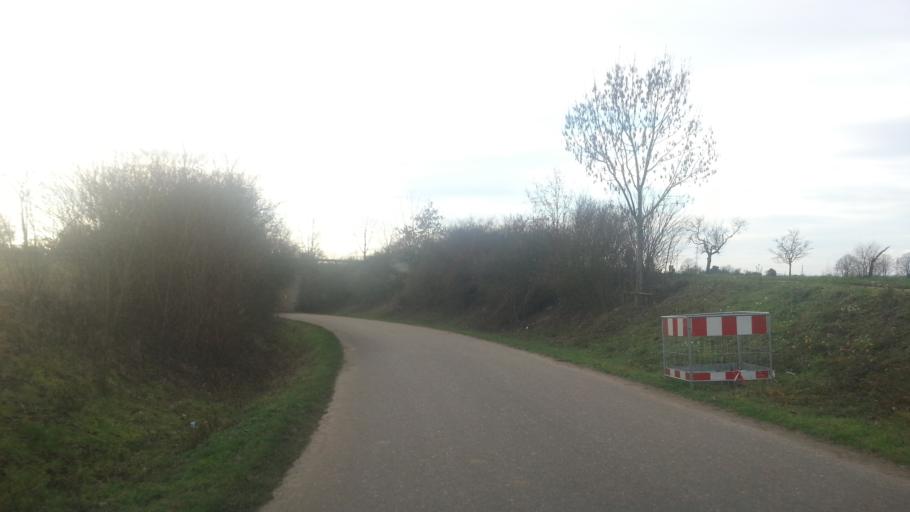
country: DE
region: Baden-Wuerttemberg
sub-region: Karlsruhe Region
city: Eppelheim
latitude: 49.3759
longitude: 8.6536
